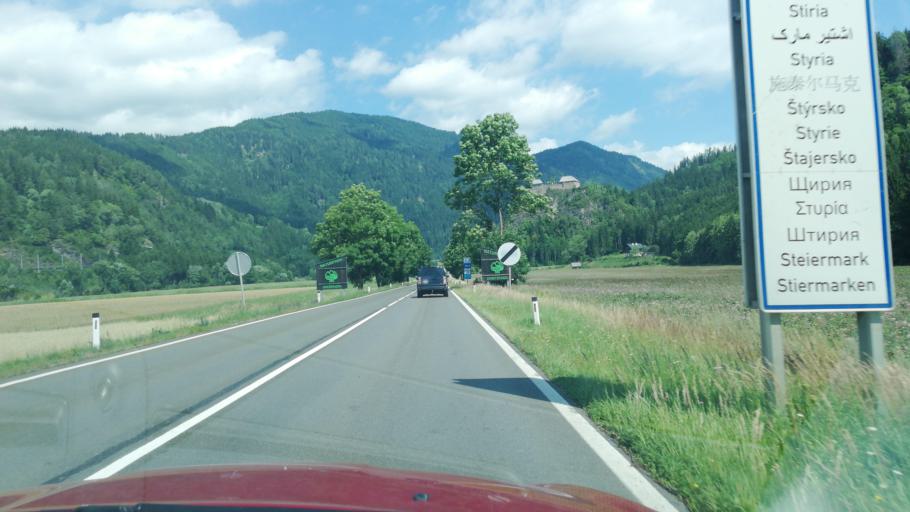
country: AT
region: Styria
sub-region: Politischer Bezirk Murau
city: Durnstein in der Steiermark
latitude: 46.9824
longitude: 14.3914
